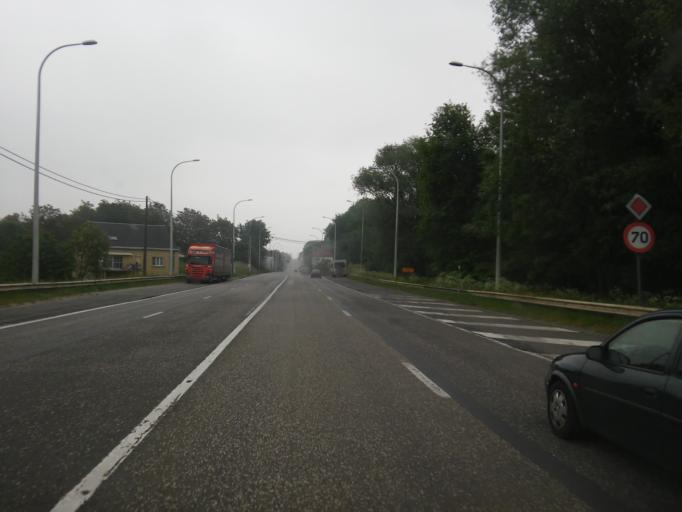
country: BE
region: Flanders
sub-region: Provincie Vlaams-Brabant
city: Lennik
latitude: 50.8354
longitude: 4.1533
